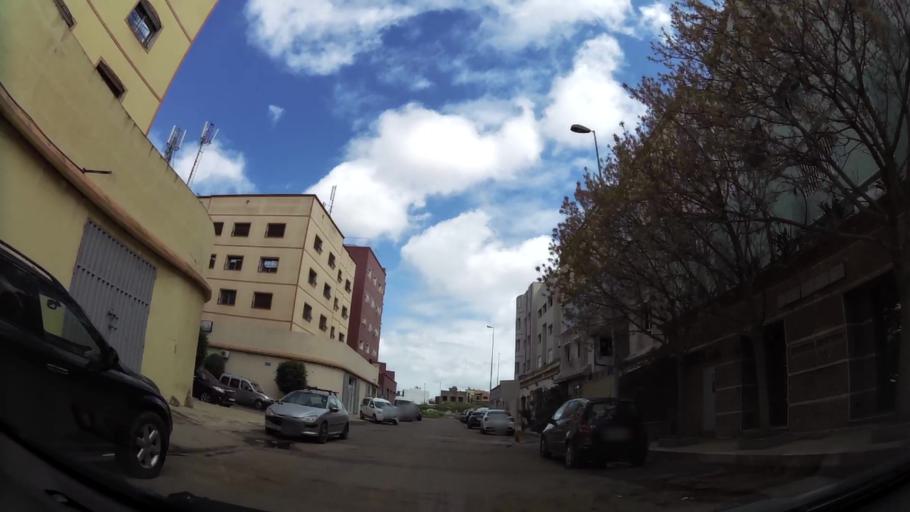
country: MA
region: Grand Casablanca
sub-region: Casablanca
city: Casablanca
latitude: 33.5292
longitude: -7.6013
